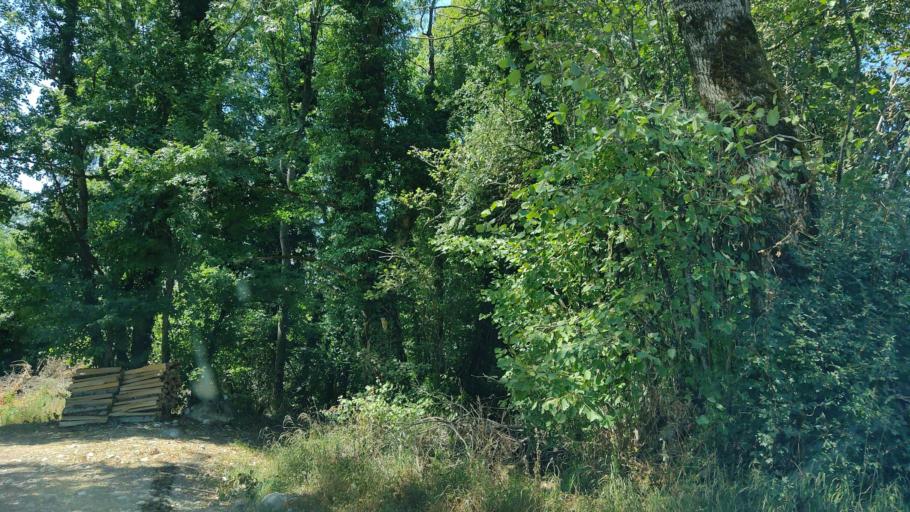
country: FR
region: Rhone-Alpes
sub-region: Departement de la Savoie
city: Novalaise
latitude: 45.6111
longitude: 5.7821
